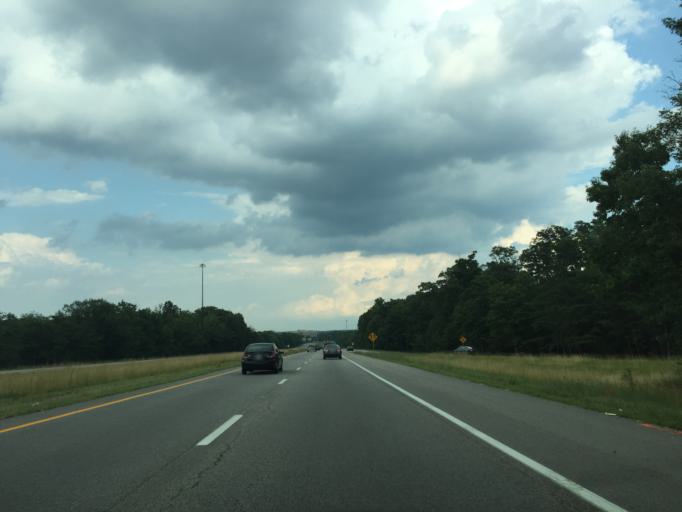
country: US
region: Maryland
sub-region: Prince George's County
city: West Laurel
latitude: 39.1006
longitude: -76.8841
